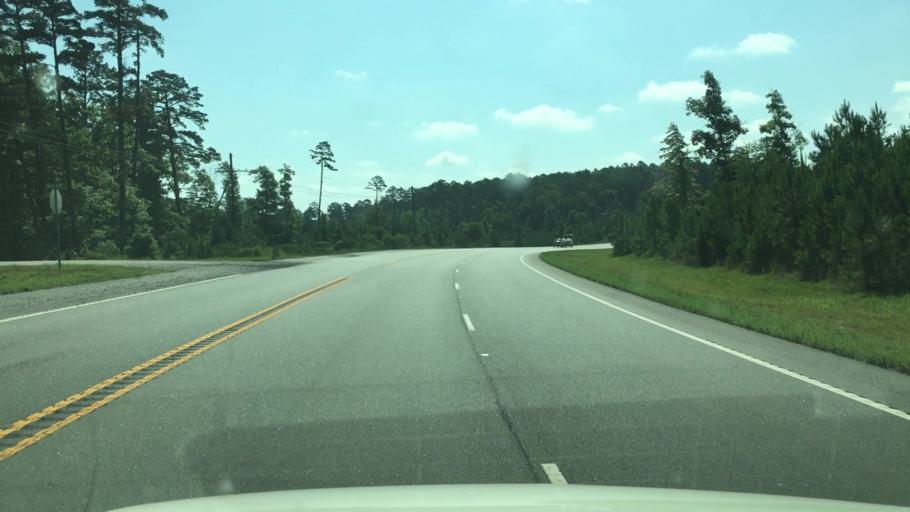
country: US
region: Arkansas
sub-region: Garland County
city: Piney
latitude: 34.5229
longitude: -93.3212
